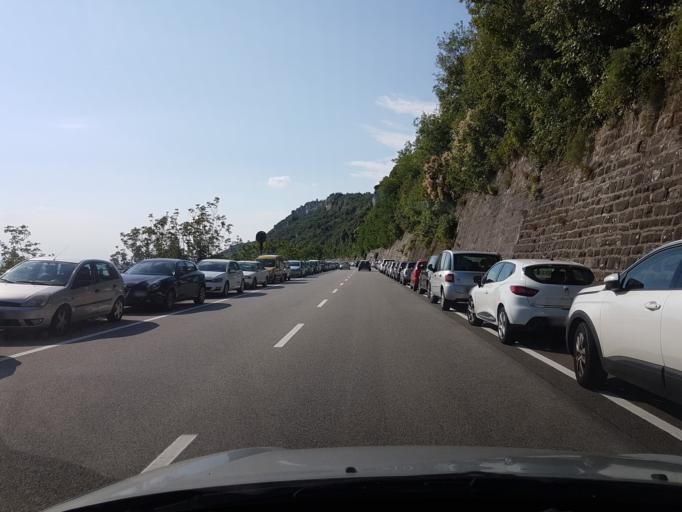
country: IT
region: Friuli Venezia Giulia
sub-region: Provincia di Trieste
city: Aurisina Cave
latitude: 45.7481
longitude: 13.6607
